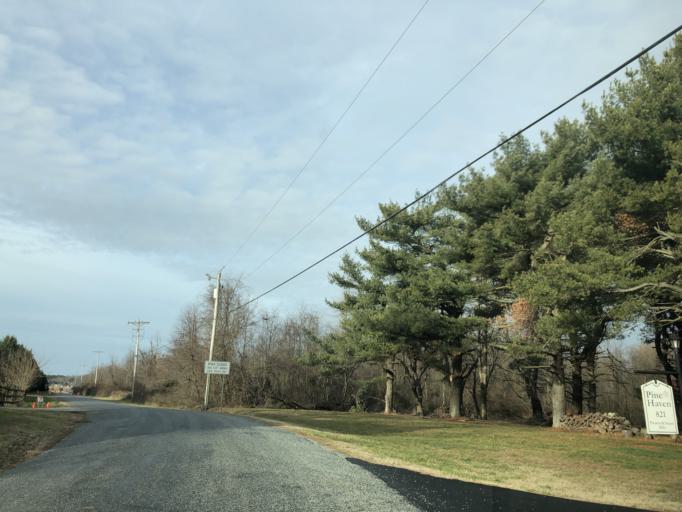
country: US
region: Delaware
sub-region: New Castle County
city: Middletown
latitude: 39.4534
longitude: -75.6402
